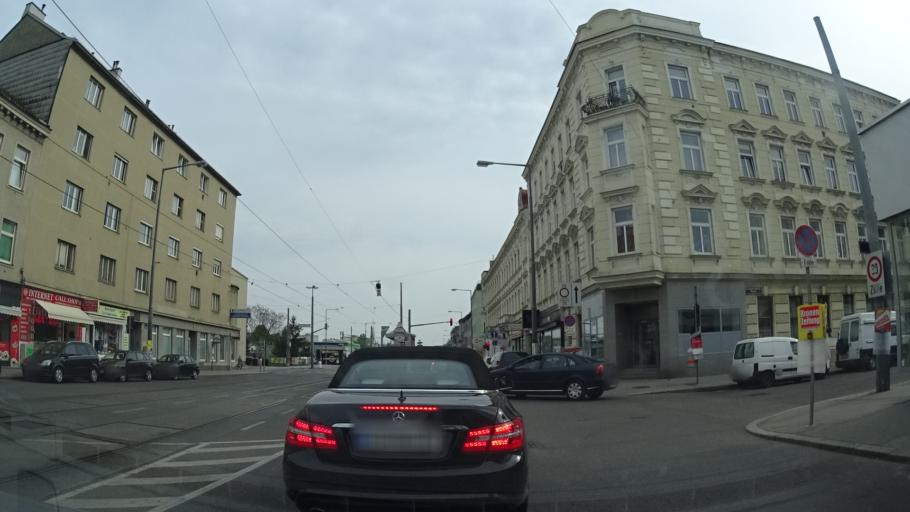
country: AT
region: Lower Austria
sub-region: Politischer Bezirk Korneuburg
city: Langenzersdorf
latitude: 48.2667
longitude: 16.3929
